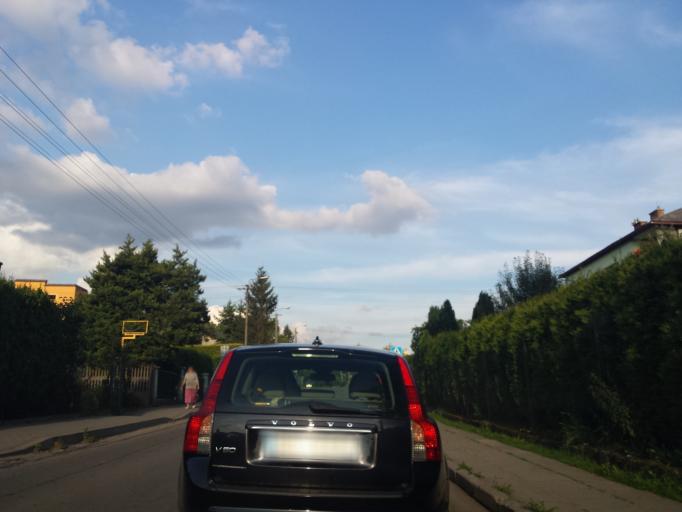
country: PL
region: Silesian Voivodeship
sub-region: Powiat bielski
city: Wilkowice
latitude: 49.7602
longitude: 19.1022
